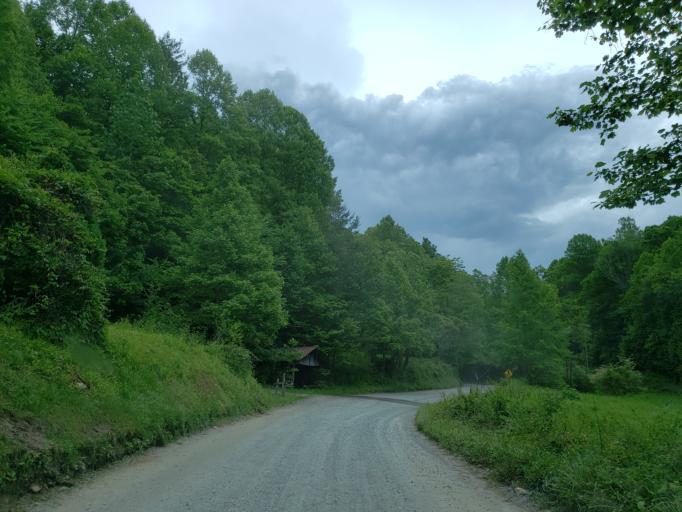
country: US
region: Georgia
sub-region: Fannin County
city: Blue Ridge
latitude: 34.8397
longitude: -84.4141
